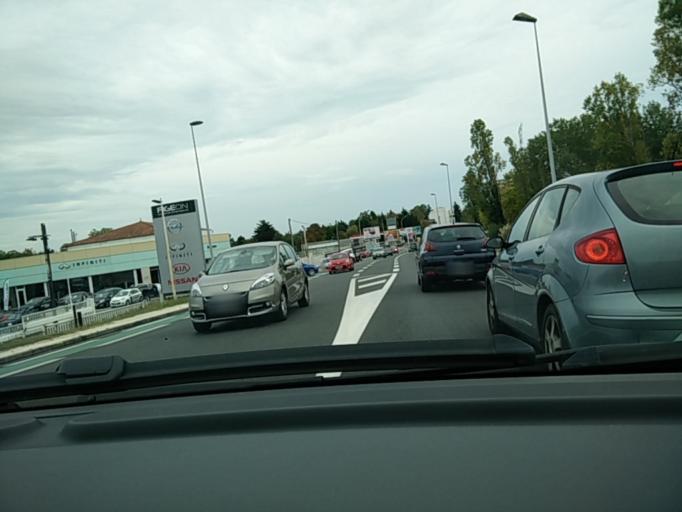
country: FR
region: Aquitaine
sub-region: Departement de la Gironde
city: Bruges
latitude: 44.8789
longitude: -0.6256
